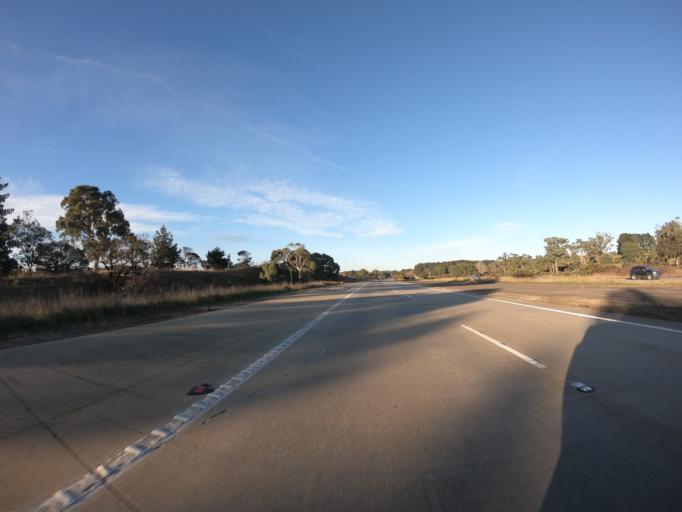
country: AU
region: New South Wales
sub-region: Yass Valley
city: Gundaroo
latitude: -35.1361
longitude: 149.3392
